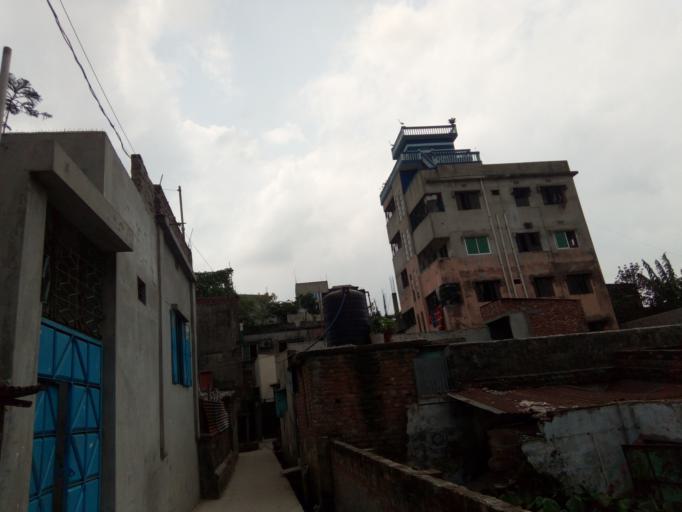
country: BD
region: Dhaka
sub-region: Dhaka
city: Dhaka
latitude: 23.6921
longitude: 90.4464
